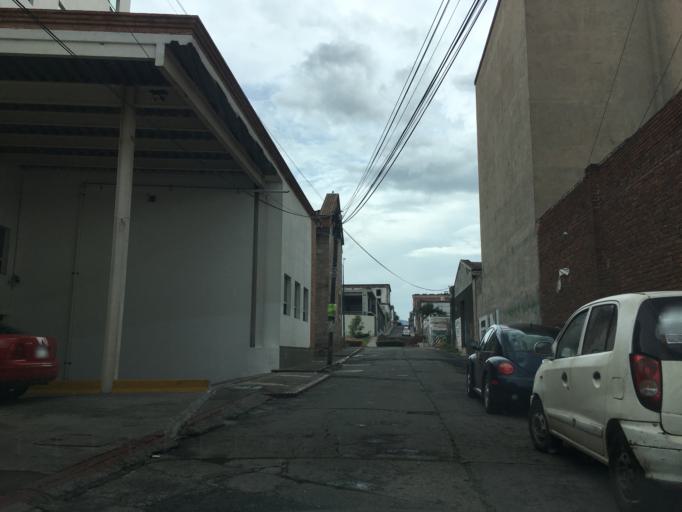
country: MX
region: Michoacan
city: Morelia
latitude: 19.7078
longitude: -101.1968
